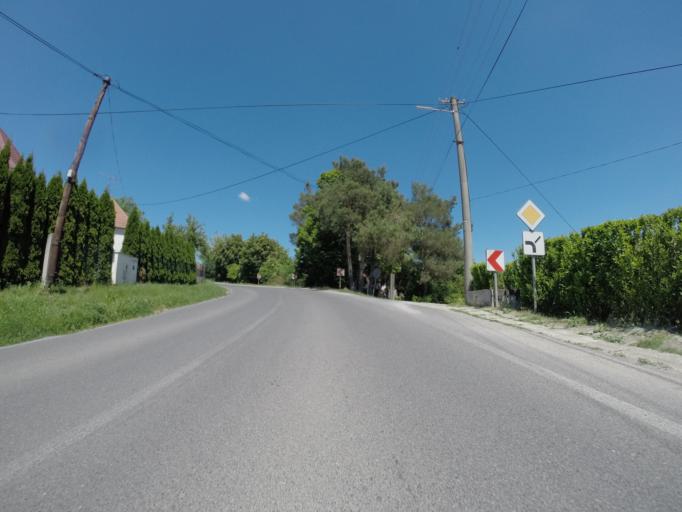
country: SK
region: Trnavsky
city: Hlohovec
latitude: 48.4646
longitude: 17.9487
